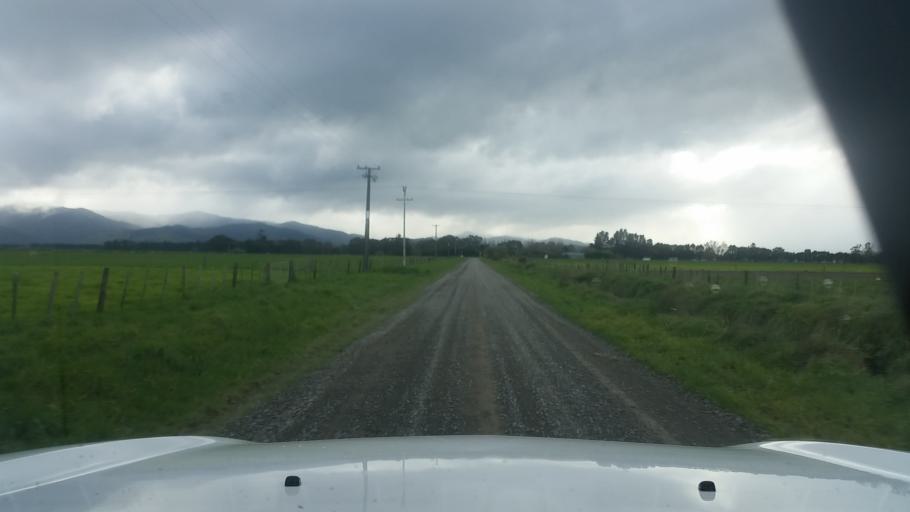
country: NZ
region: Wellington
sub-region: South Wairarapa District
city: Waipawa
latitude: -41.1478
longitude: 175.4196
